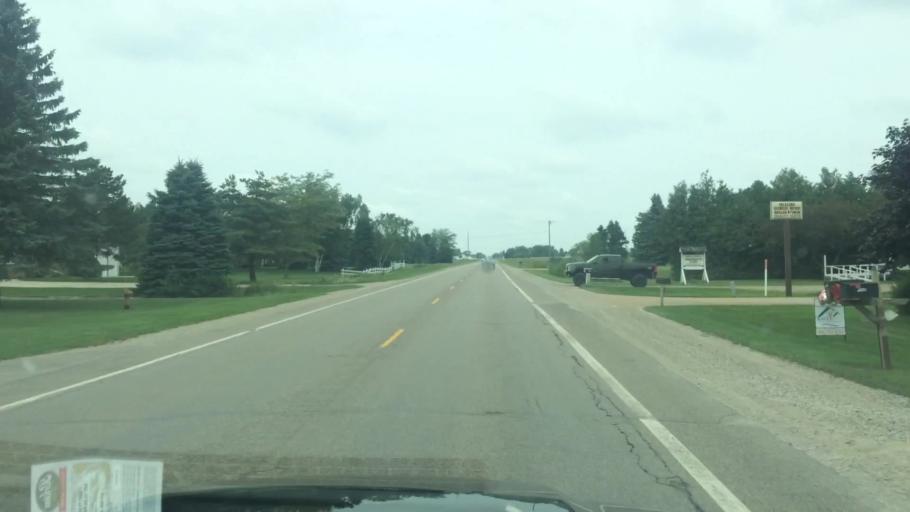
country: US
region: Michigan
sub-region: Huron County
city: Bad Axe
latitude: 43.8293
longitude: -83.0012
